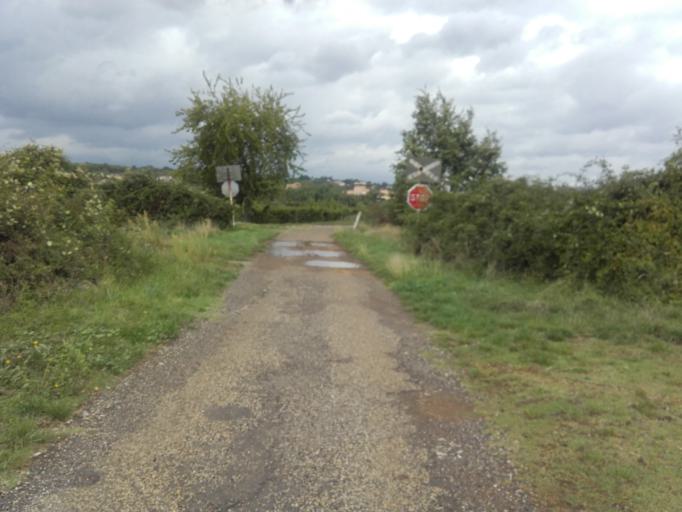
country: FR
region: Rhone-Alpes
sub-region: Departement de l'Ardeche
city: Lavilledieu
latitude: 44.5573
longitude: 4.4491
